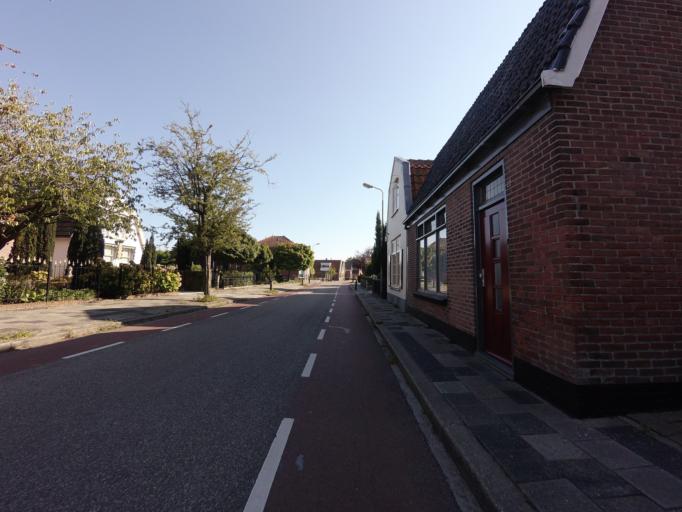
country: NL
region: North Holland
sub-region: Gemeente Enkhuizen
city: Enkhuizen
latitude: 52.6981
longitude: 5.2524
